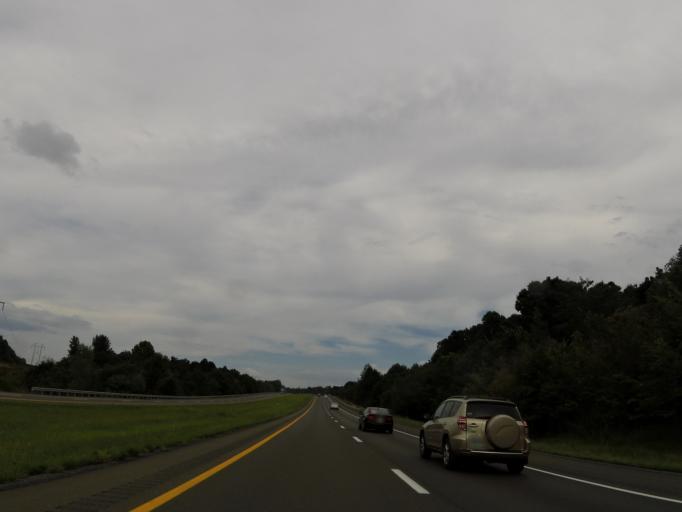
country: US
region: Kentucky
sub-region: Lyon County
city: Eddyville
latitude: 37.0692
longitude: -88.1541
